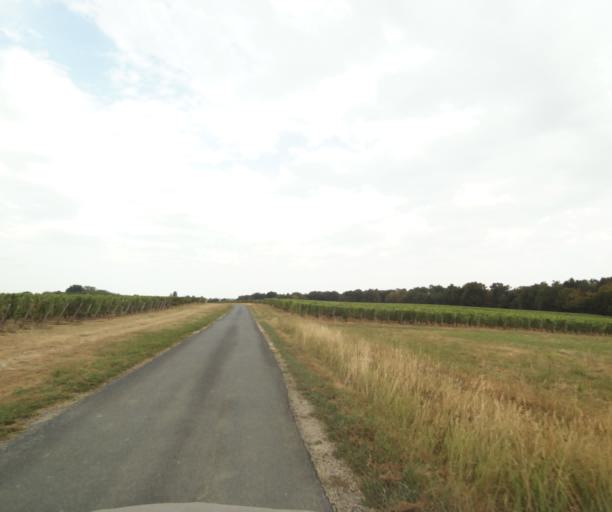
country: FR
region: Aquitaine
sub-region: Departement de la Gironde
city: Creon
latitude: 44.7516
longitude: -0.3399
